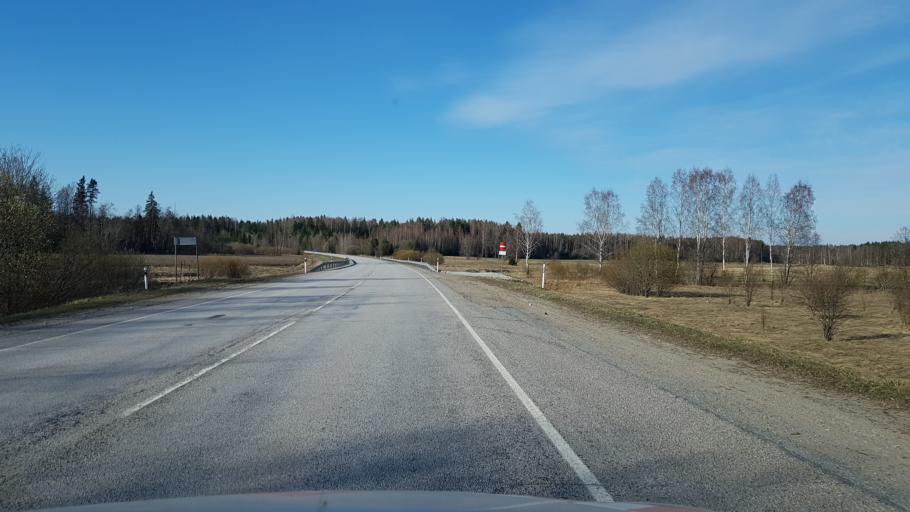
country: EE
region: Ida-Virumaa
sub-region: Johvi vald
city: Johvi
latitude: 59.1479
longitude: 27.3586
